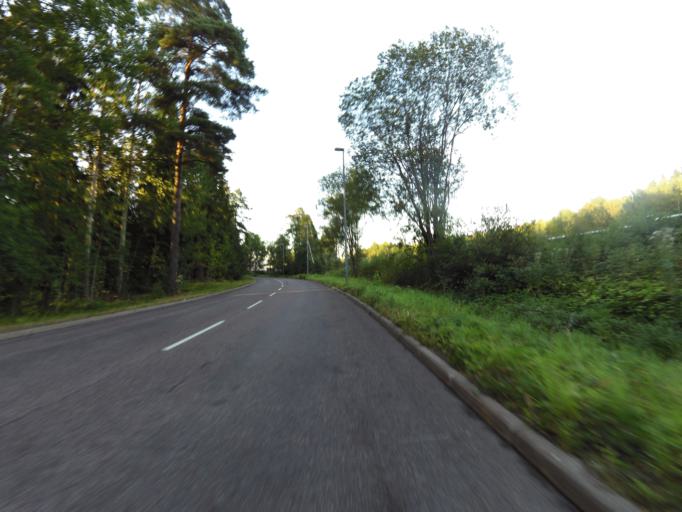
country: SE
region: Gaevleborg
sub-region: Gavle Kommun
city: Gavle
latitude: 60.6522
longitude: 17.1537
